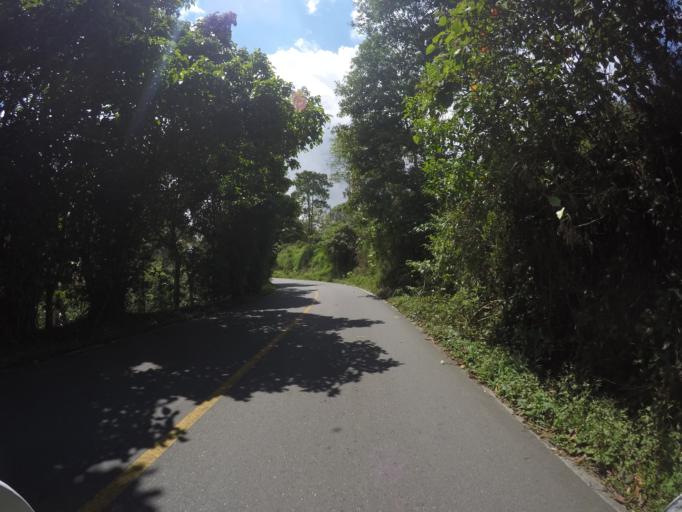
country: CO
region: Quindio
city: Filandia
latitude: 4.6479
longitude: -75.6795
